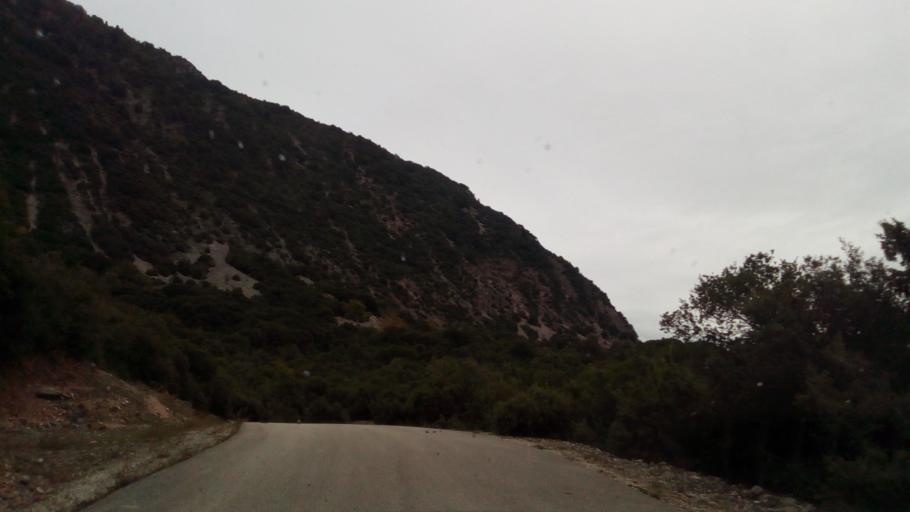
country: GR
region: West Greece
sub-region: Nomos Aitolias kai Akarnanias
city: Thermo
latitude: 38.6156
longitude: 21.8422
